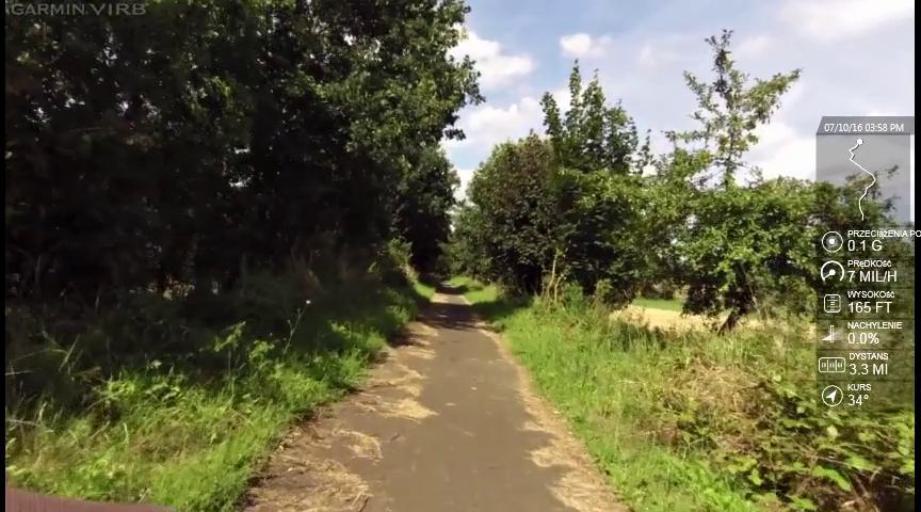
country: PL
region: West Pomeranian Voivodeship
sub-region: Powiat gryfinski
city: Banie
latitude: 53.1521
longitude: 14.6277
